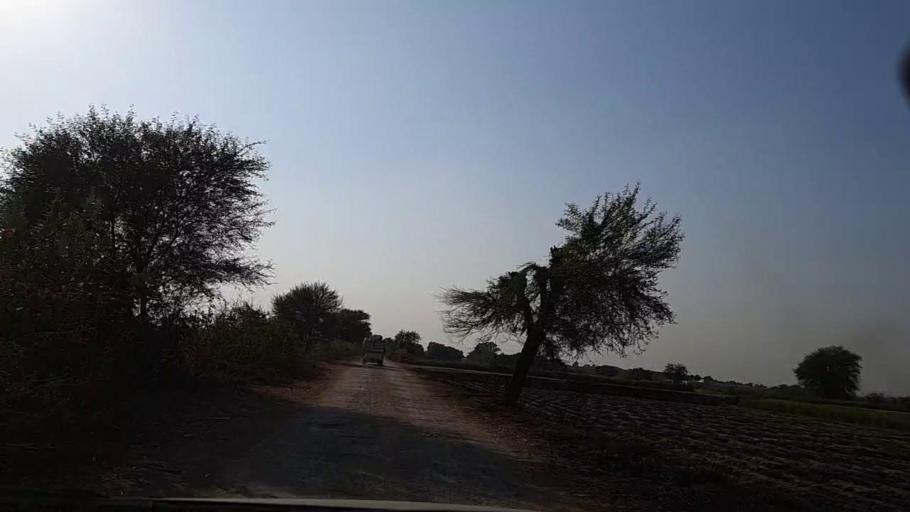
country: PK
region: Sindh
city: Tando Ghulam Ali
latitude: 25.2240
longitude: 68.9560
